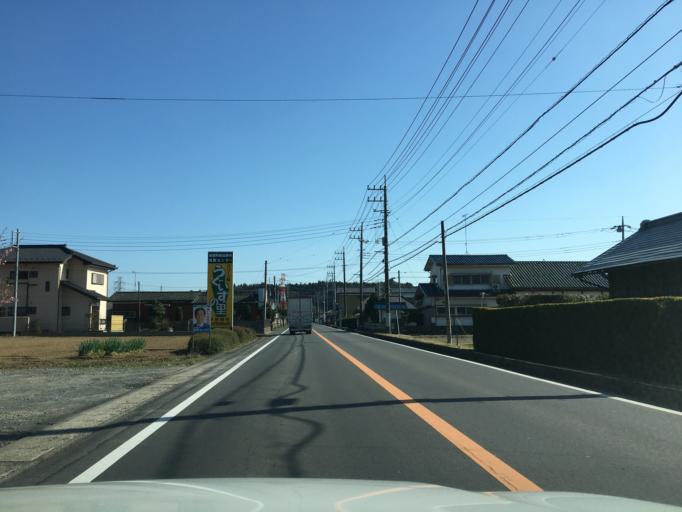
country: JP
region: Ibaraki
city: Omiya
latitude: 36.4939
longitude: 140.3740
